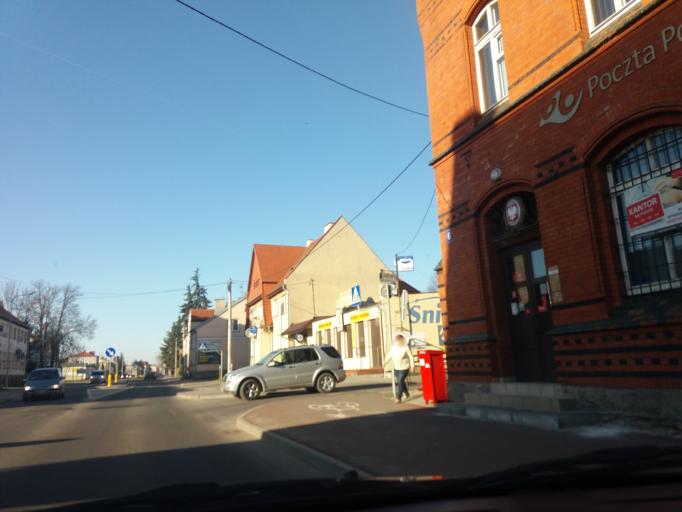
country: PL
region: Warmian-Masurian Voivodeship
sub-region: Powiat nidzicki
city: Nidzica
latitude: 53.3621
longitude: 20.4262
